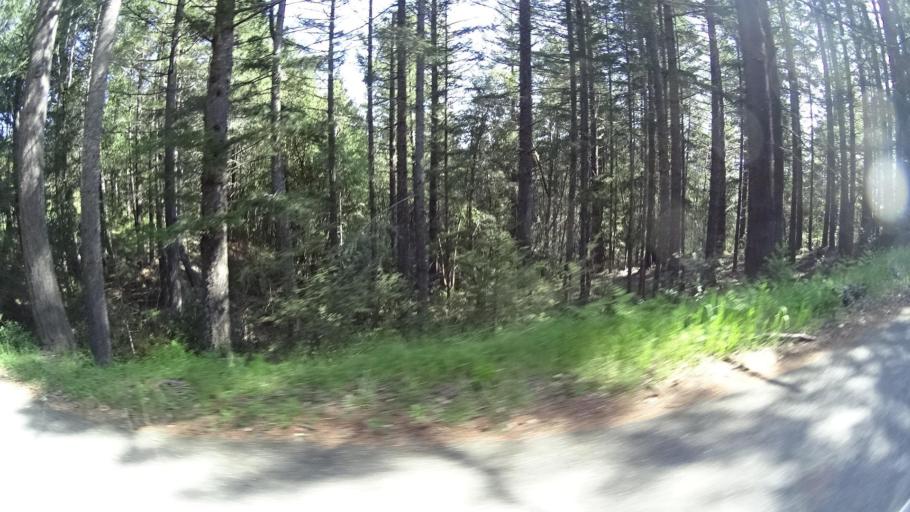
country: US
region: California
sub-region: Humboldt County
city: Redway
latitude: 40.0718
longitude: -123.6500
